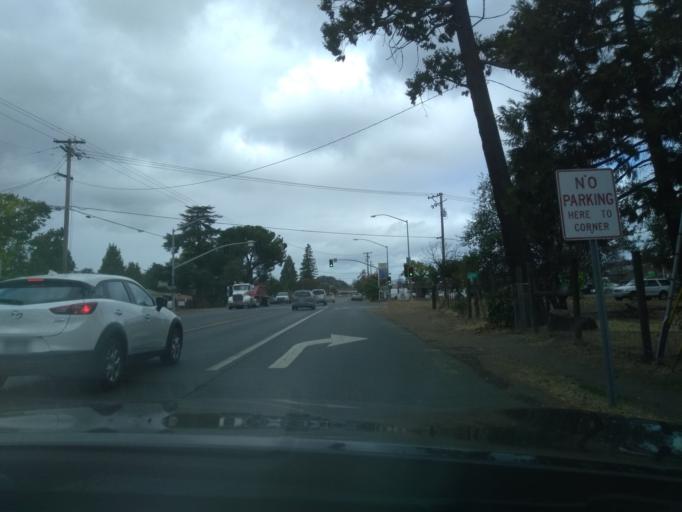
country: US
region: California
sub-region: Mendocino County
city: Ukiah
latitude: 39.1922
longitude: -123.2069
